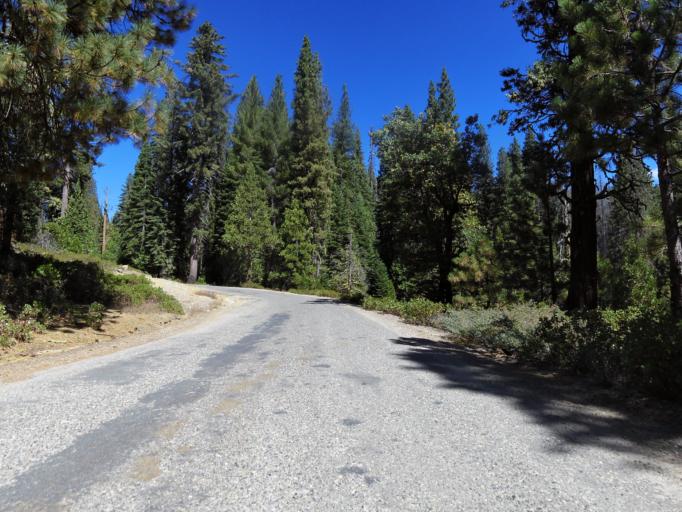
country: US
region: California
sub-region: Madera County
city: Oakhurst
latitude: 37.4373
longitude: -119.5410
